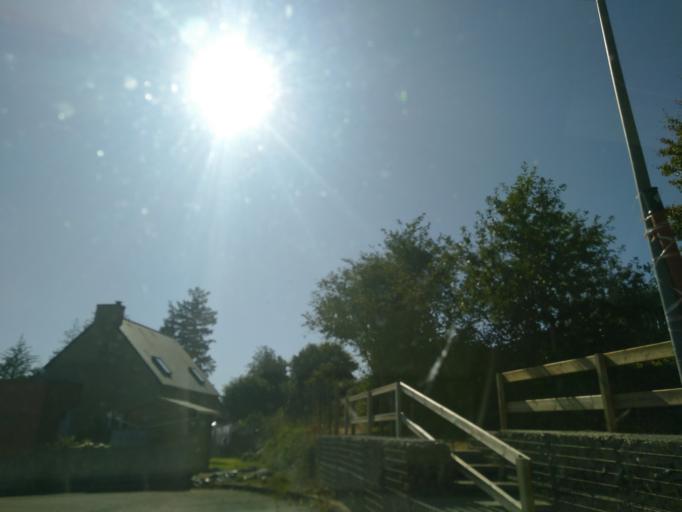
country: FR
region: Brittany
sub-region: Departement du Finistere
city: Le Faou
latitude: 48.2630
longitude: -4.1915
